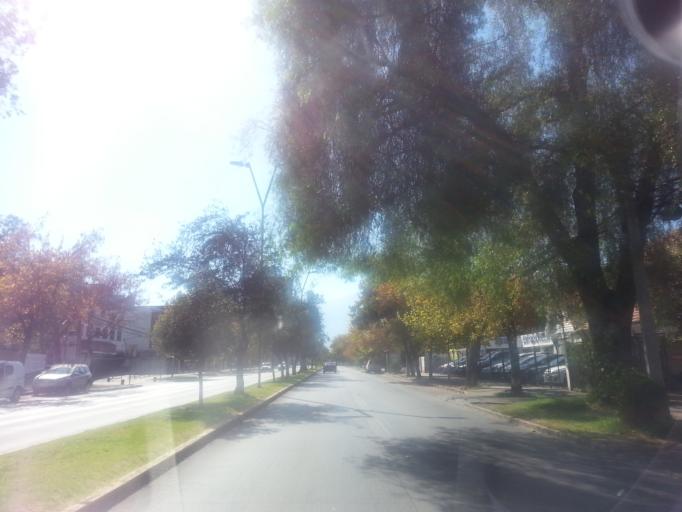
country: CL
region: Santiago Metropolitan
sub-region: Provincia de Santiago
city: Villa Presidente Frei, Nunoa, Santiago, Chile
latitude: -33.4356
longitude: -70.5915
